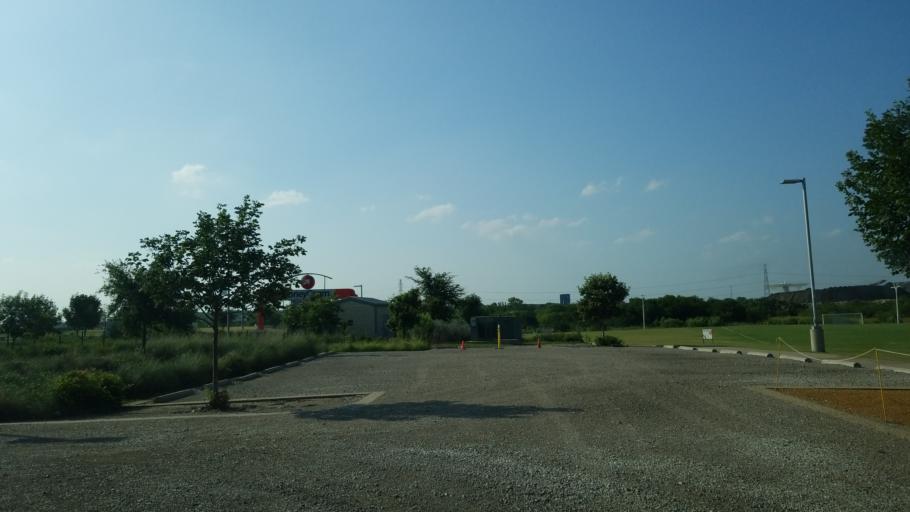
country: US
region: Texas
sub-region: Dallas County
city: Farmers Branch
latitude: 32.8797
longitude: -96.9049
